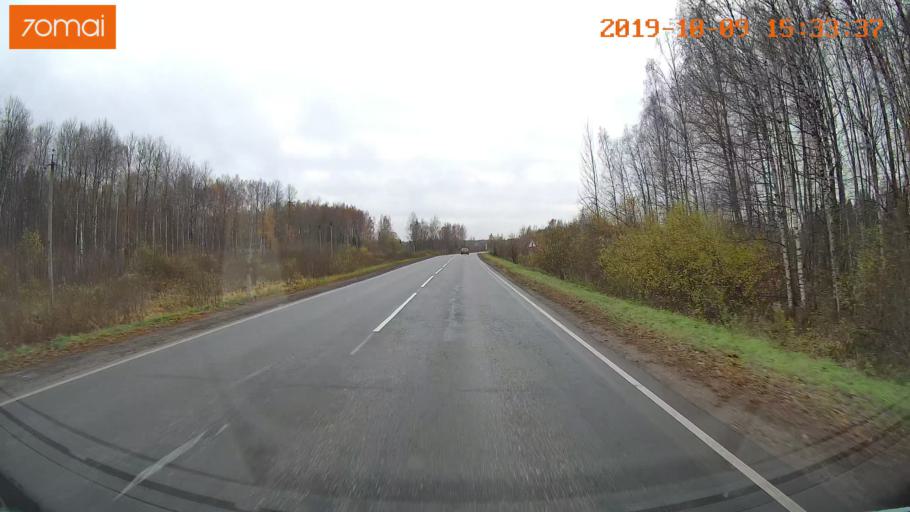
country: RU
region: Kostroma
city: Oktyabr'skiy
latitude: 57.9492
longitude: 41.2598
